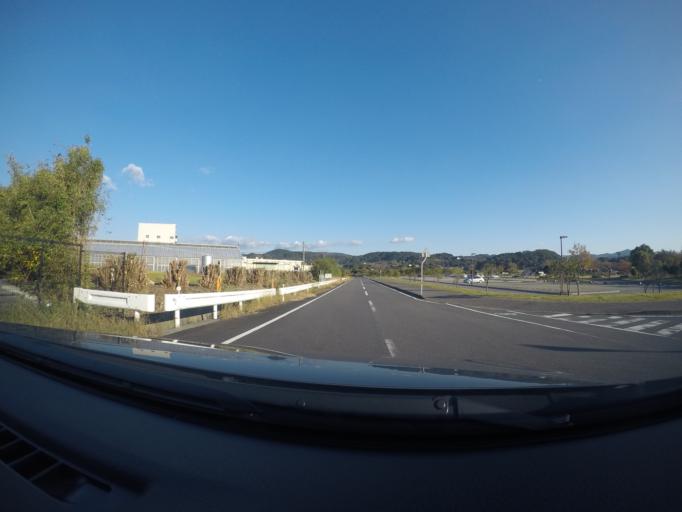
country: JP
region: Kumamoto
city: Minamata
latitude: 32.2030
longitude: 130.3784
